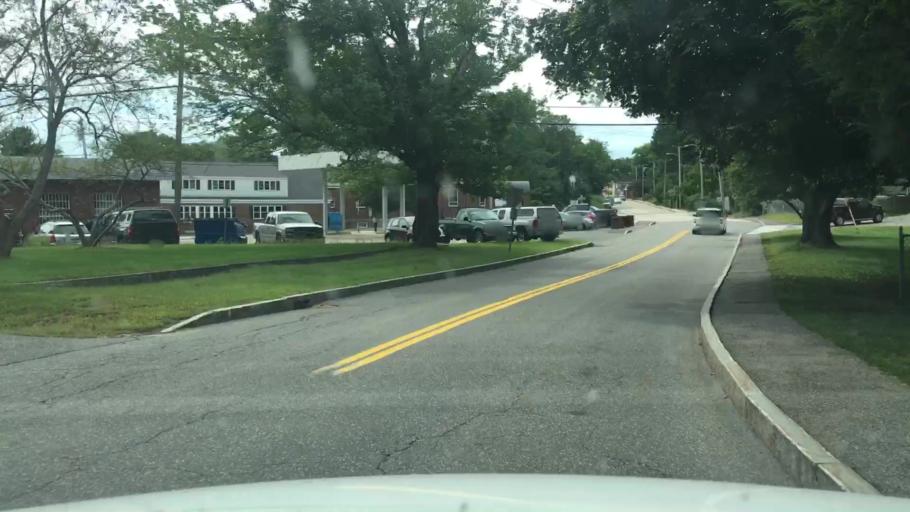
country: US
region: Maine
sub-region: York County
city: Kittery
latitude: 43.0894
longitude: -70.7406
